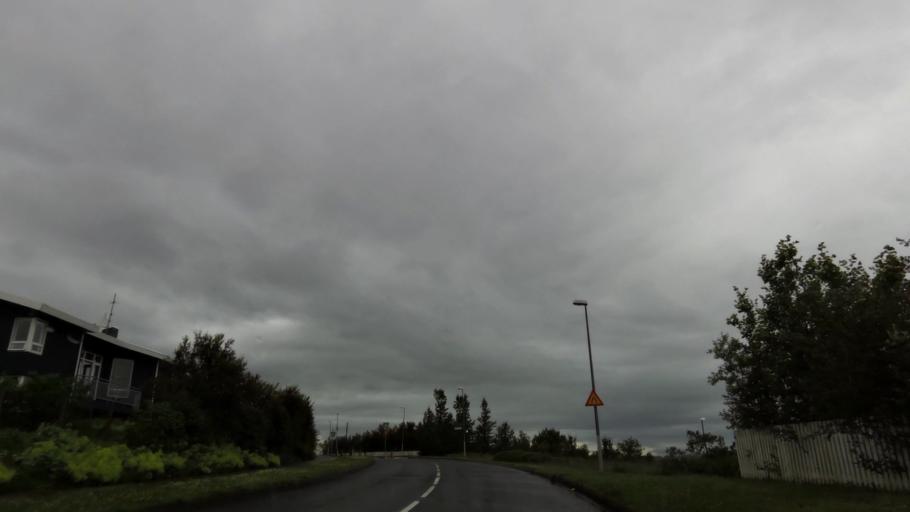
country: IS
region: Capital Region
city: Mosfellsbaer
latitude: 64.1374
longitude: -21.7777
